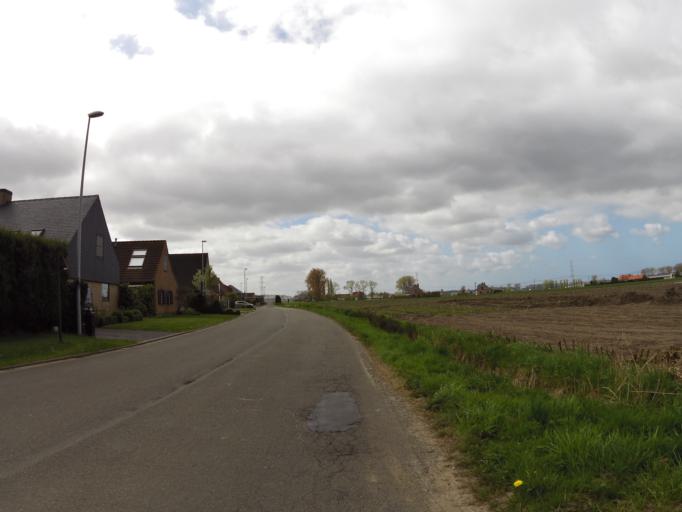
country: BE
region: Flanders
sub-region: Provincie West-Vlaanderen
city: Jabbeke
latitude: 51.1933
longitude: 3.1341
